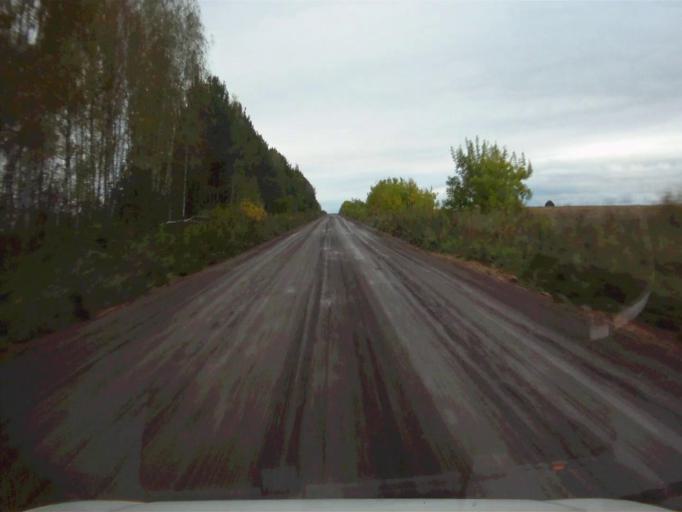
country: RU
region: Sverdlovsk
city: Mikhaylovsk
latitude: 56.1536
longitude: 59.2635
